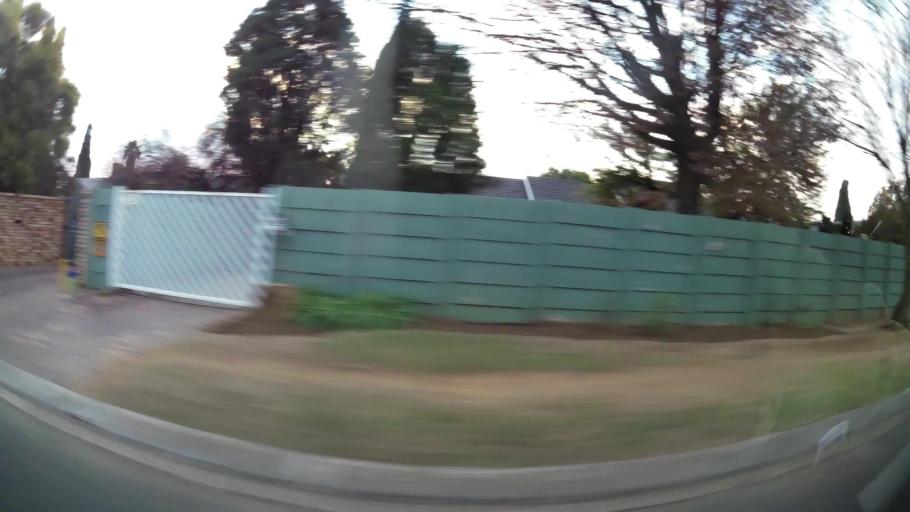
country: ZA
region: Gauteng
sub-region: Ekurhuleni Metropolitan Municipality
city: Benoni
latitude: -26.1691
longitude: 28.3054
